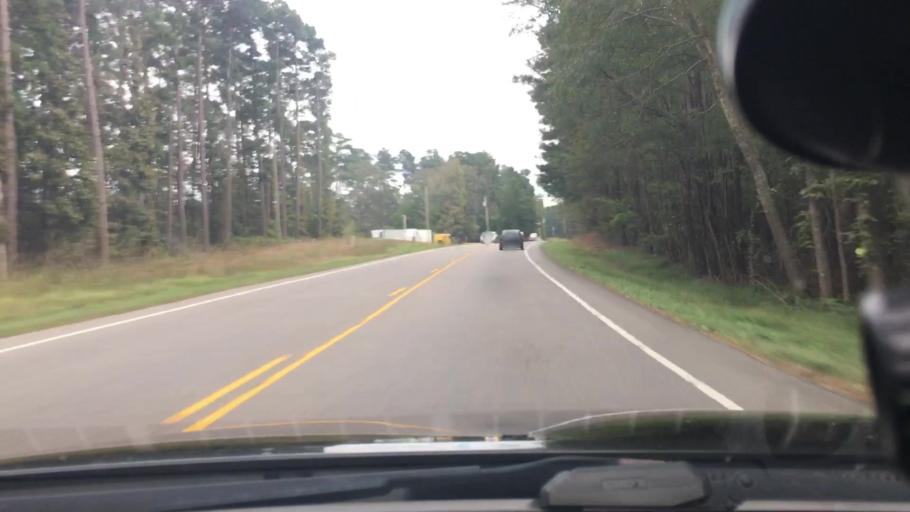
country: US
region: North Carolina
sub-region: Moore County
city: Carthage
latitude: 35.3803
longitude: -79.4776
